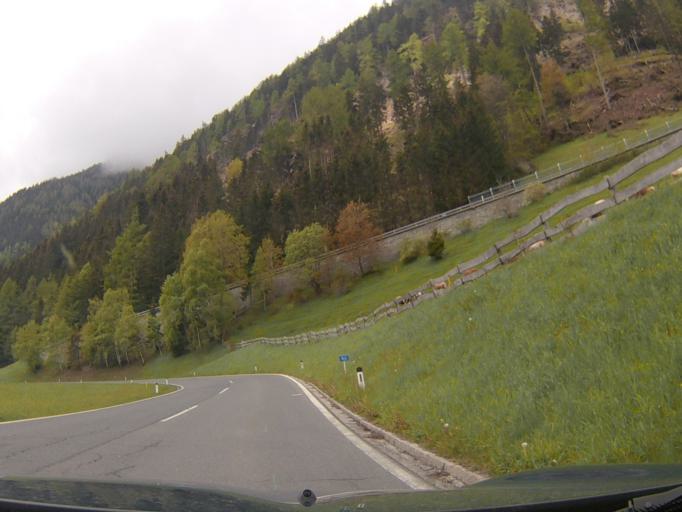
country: AT
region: Carinthia
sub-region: Politischer Bezirk Spittal an der Drau
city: Obervellach
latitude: 46.9658
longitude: 13.1832
